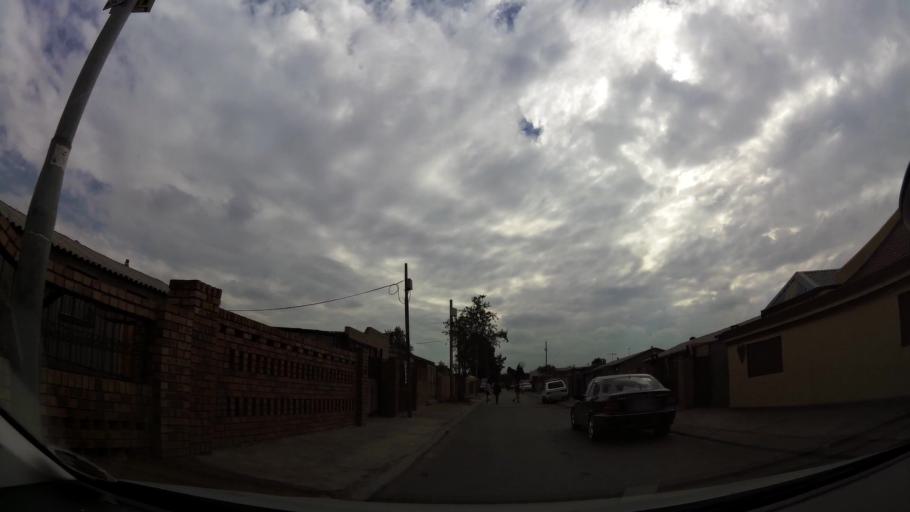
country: ZA
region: Gauteng
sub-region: City of Johannesburg Metropolitan Municipality
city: Soweto
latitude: -26.2718
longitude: 27.8592
